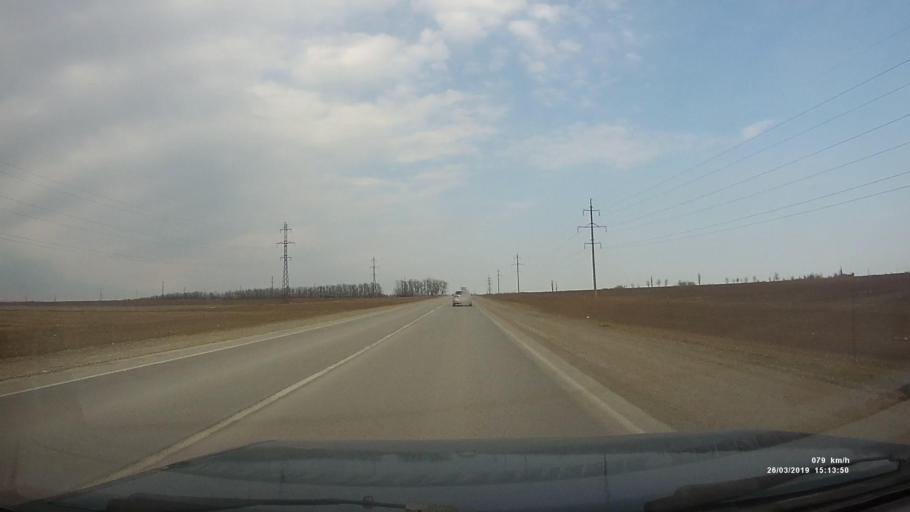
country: RU
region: Rostov
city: Taganrog
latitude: 47.2770
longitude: 38.8606
